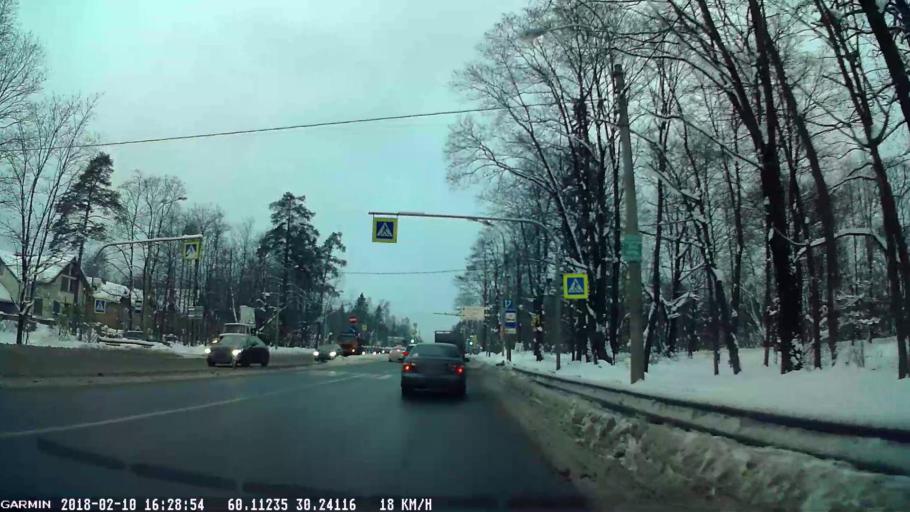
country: RU
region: St.-Petersburg
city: Levashovo
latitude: 60.1125
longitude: 30.2411
